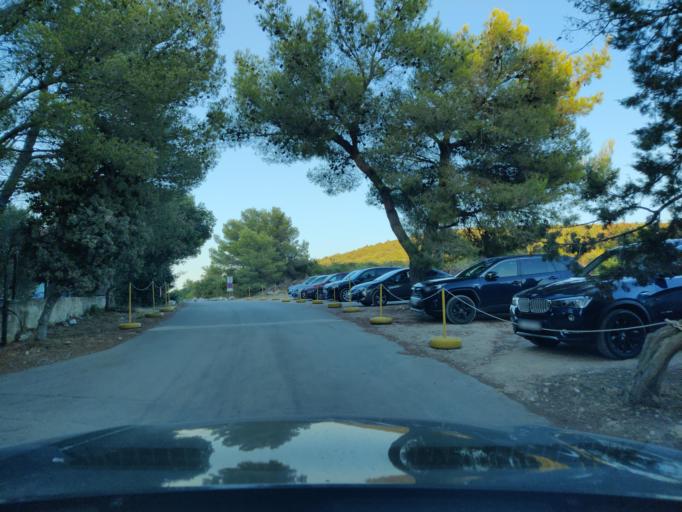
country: HR
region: Sibensko-Kniniska
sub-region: Grad Sibenik
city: Tisno
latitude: 43.8092
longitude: 15.6286
